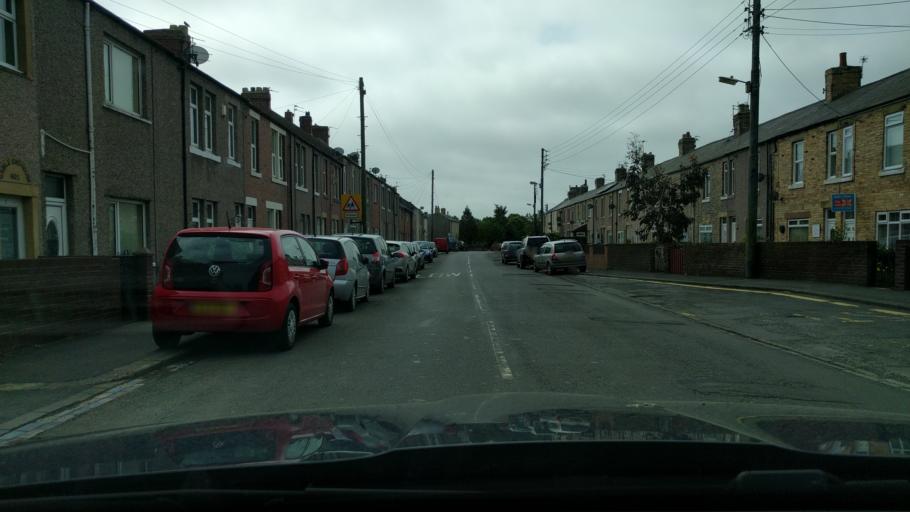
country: GB
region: England
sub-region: Northumberland
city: East Chevington
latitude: 55.2862
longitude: -1.6038
